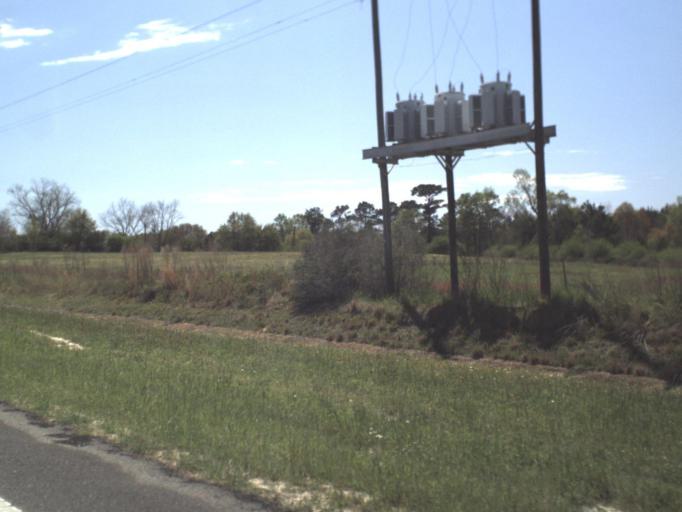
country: US
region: Florida
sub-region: Walton County
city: DeFuniak Springs
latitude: 30.7646
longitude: -85.9589
